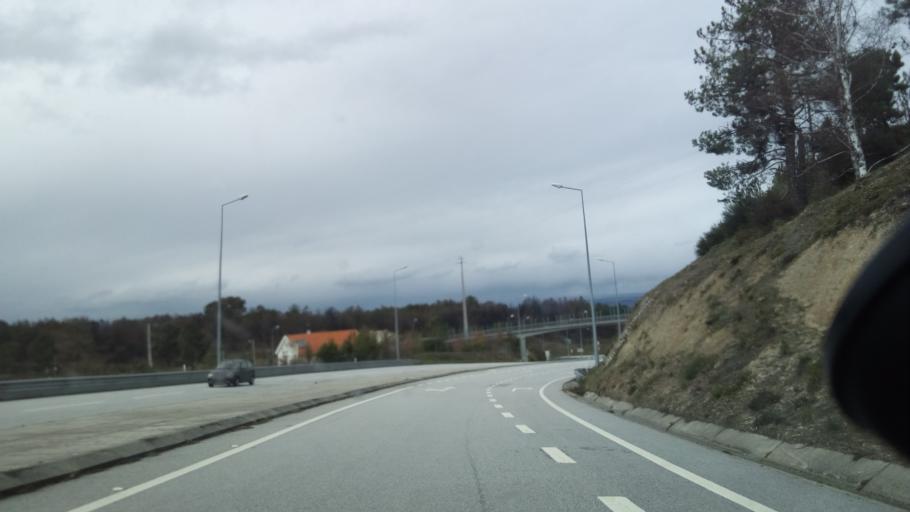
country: PT
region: Guarda
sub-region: Manteigas
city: Manteigas
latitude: 40.4745
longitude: -7.6000
